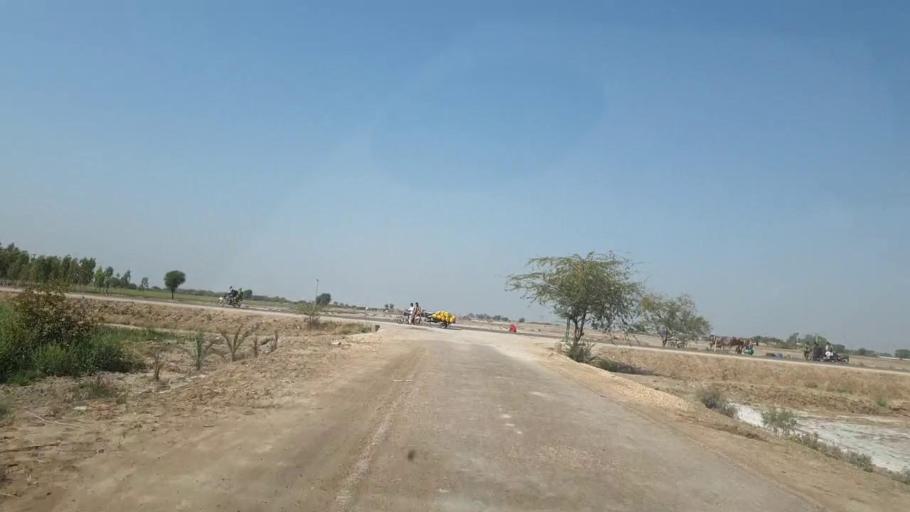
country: PK
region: Sindh
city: Mirpur Khas
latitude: 25.6716
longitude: 69.1067
